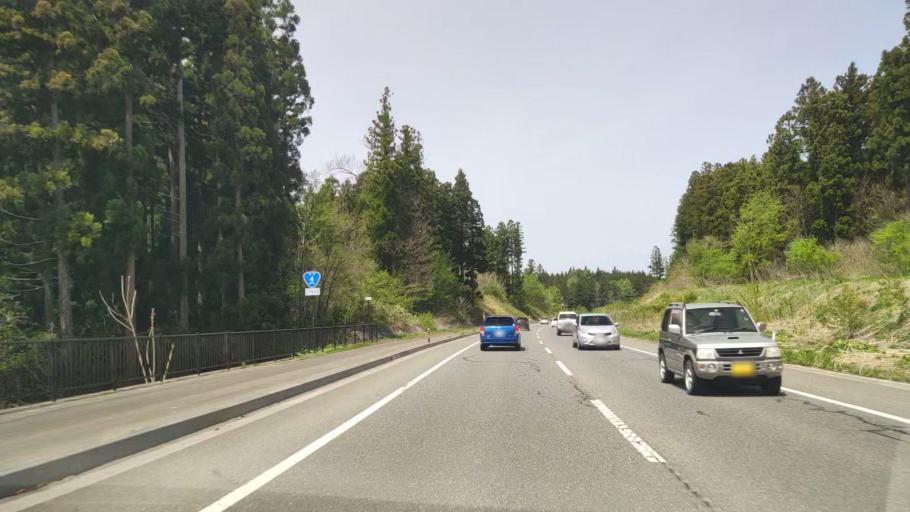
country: JP
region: Aomori
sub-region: Misawa Shi
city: Inuotose
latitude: 40.6875
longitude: 141.1694
